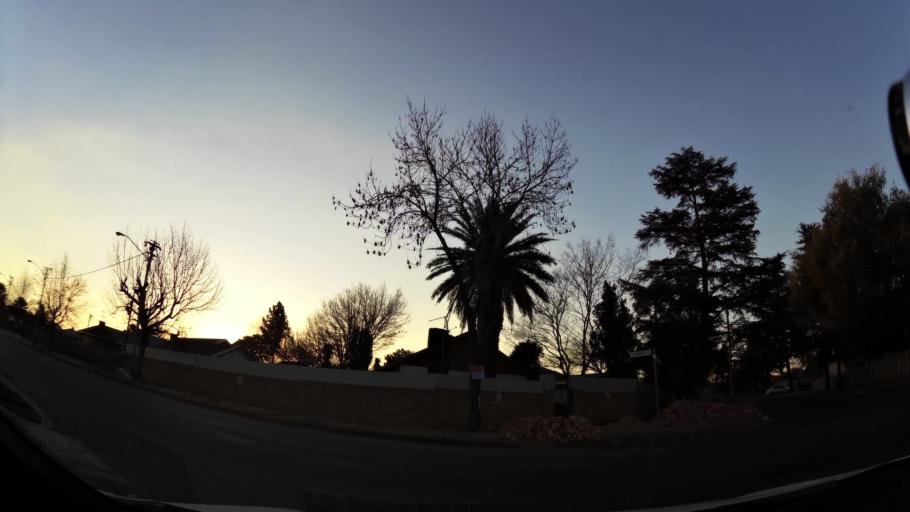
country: ZA
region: Gauteng
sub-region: Ekurhuleni Metropolitan Municipality
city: Germiston
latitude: -26.2699
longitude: 28.1593
